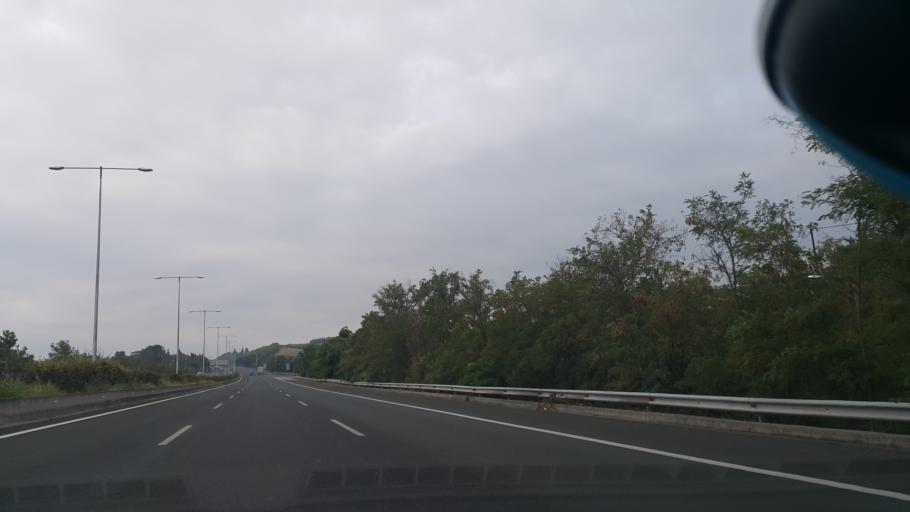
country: GR
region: Central Macedonia
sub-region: Nomos Pierias
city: Makrygialos
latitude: 40.4605
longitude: 22.5782
